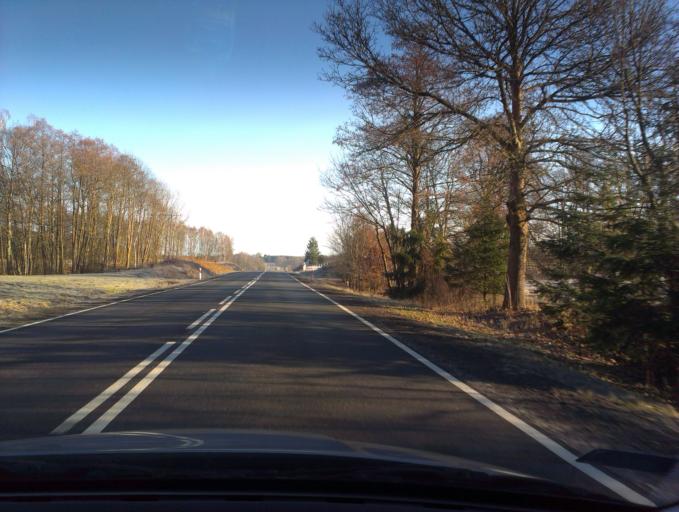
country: PL
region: West Pomeranian Voivodeship
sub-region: Powiat koszalinski
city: Bobolice
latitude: 53.8902
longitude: 16.6130
